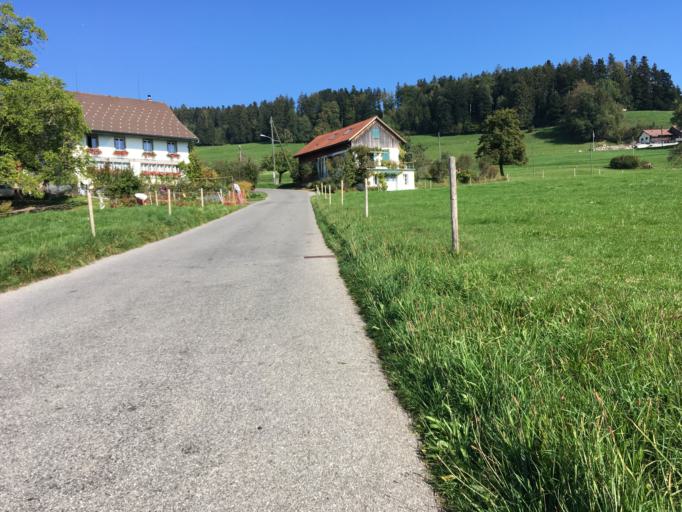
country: CH
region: Zurich
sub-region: Bezirk Hinwil
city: Baretswil
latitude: 47.3416
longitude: 8.8427
